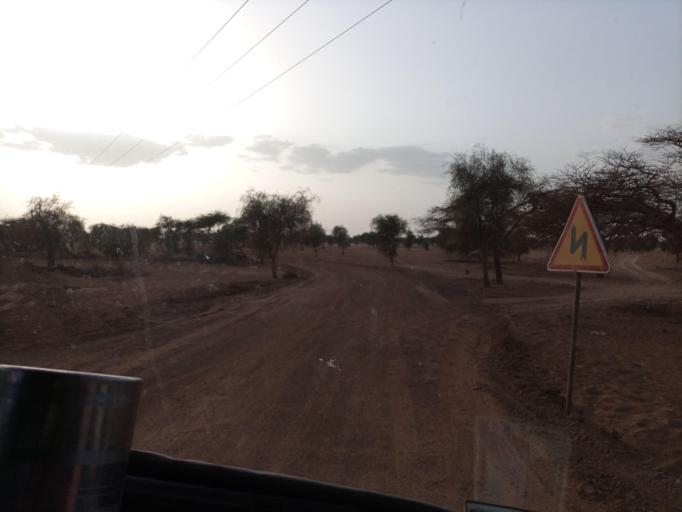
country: SN
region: Louga
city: Dara
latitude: 15.3676
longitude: -15.5668
